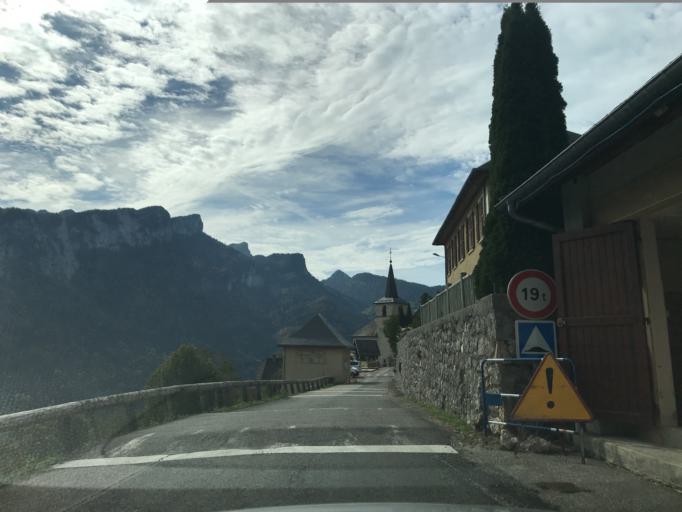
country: FR
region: Rhone-Alpes
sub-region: Departement de la Savoie
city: Les Echelles
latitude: 45.4300
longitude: 5.8254
